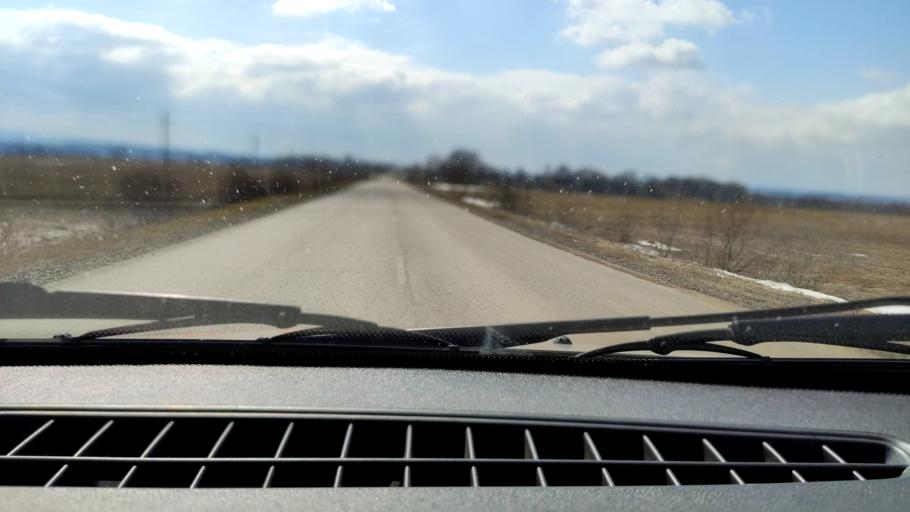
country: RU
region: Bashkortostan
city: Kudeyevskiy
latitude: 54.8383
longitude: 56.7940
